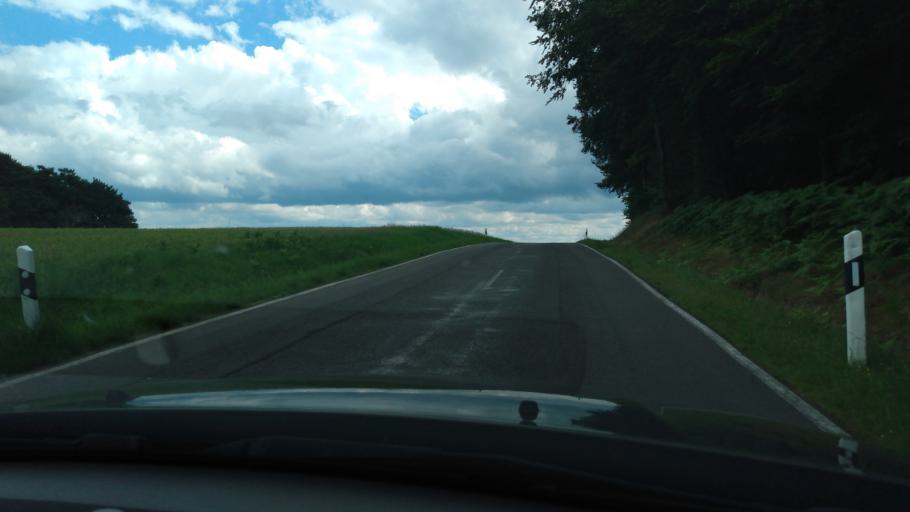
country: DE
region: Rheinland-Pfalz
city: Karl
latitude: 50.0423
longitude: 6.7871
